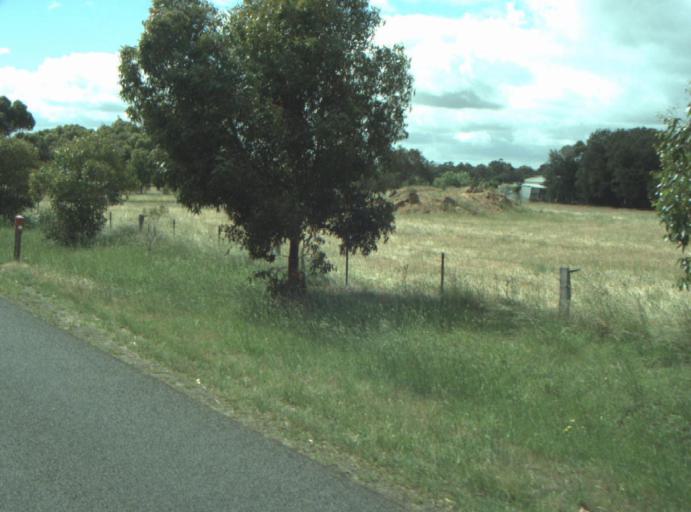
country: AU
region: Victoria
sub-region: Wyndham
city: Little River
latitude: -37.8584
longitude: 144.3781
